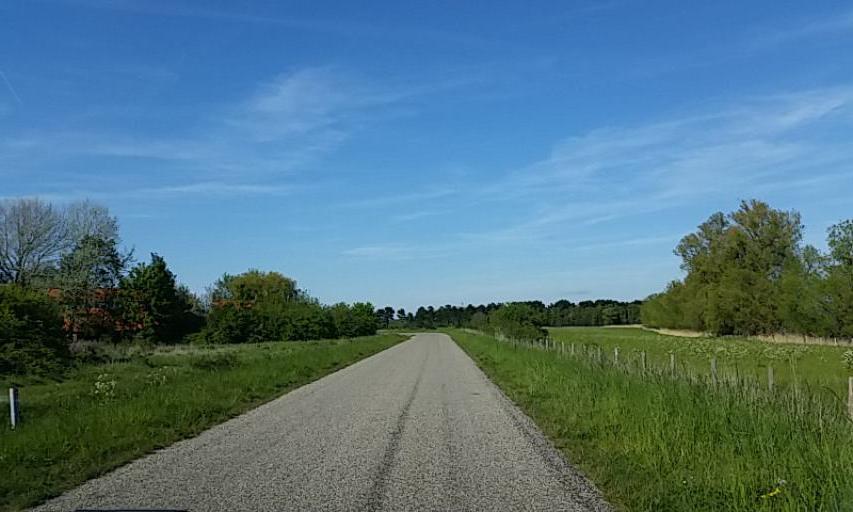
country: BE
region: Flanders
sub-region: Provincie Oost-Vlaanderen
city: Assenede
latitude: 51.3215
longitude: 3.7262
